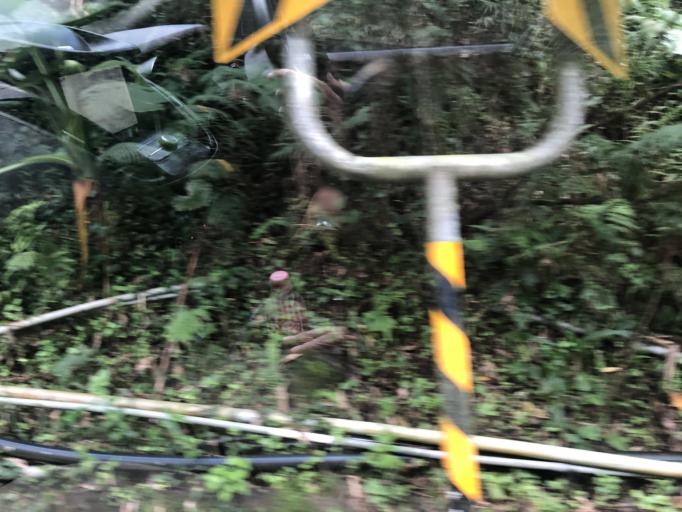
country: TW
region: Taiwan
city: Daxi
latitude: 24.8773
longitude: 121.4162
